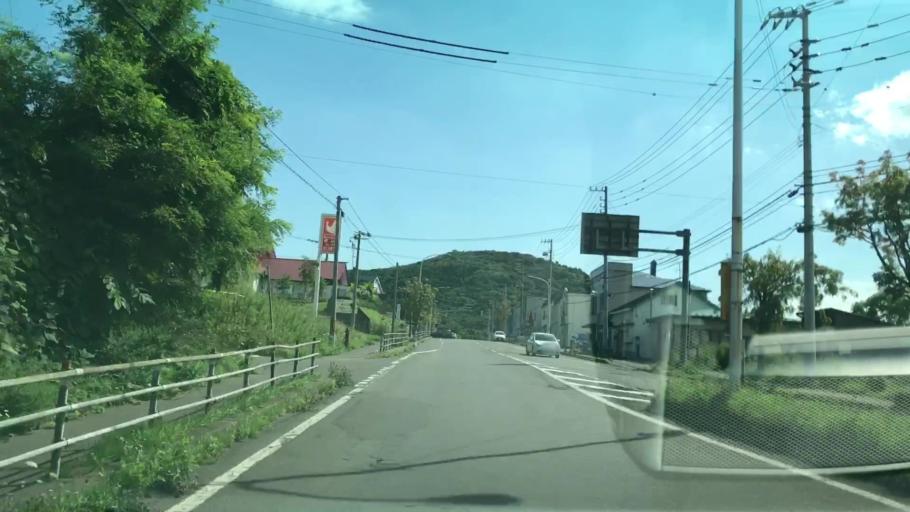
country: JP
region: Hokkaido
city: Muroran
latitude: 42.3237
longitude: 140.9967
